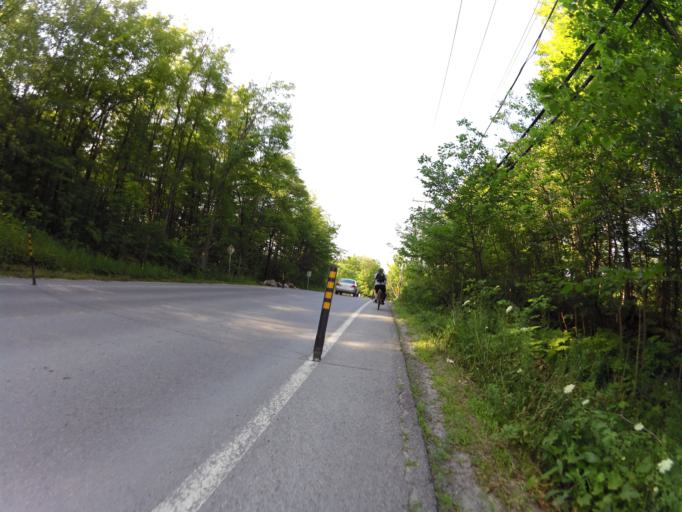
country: CA
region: Quebec
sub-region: Outaouais
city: Gatineau
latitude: 45.5022
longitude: -75.8128
